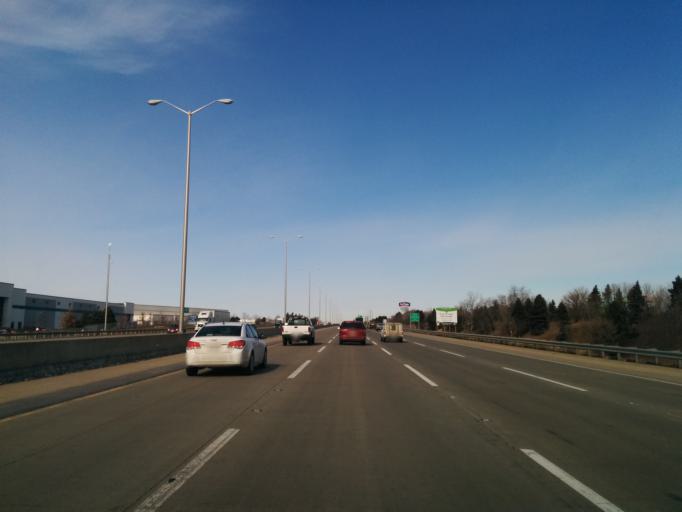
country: US
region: Illinois
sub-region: Lake County
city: Gurnee
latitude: 42.3648
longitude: -87.9394
